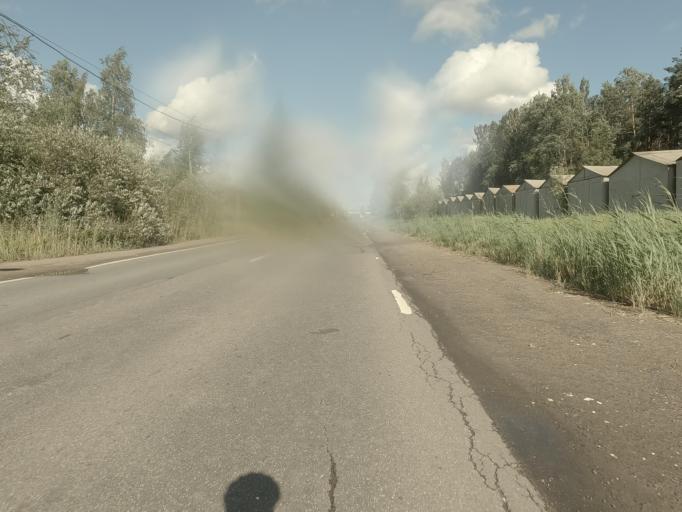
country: RU
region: St.-Petersburg
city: Krasnogvargeisky
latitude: 59.9732
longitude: 30.5223
